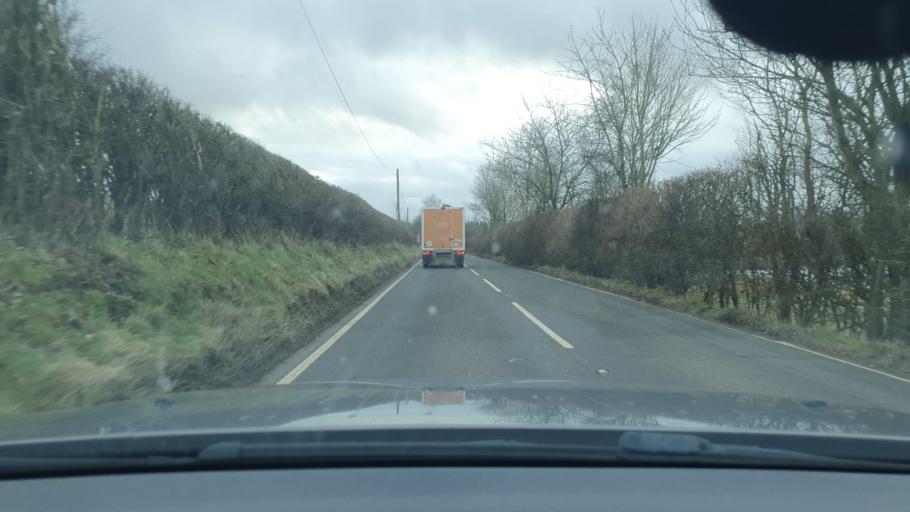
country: GB
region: England
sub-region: West Berkshire
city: Welford
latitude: 51.5013
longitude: -1.4276
